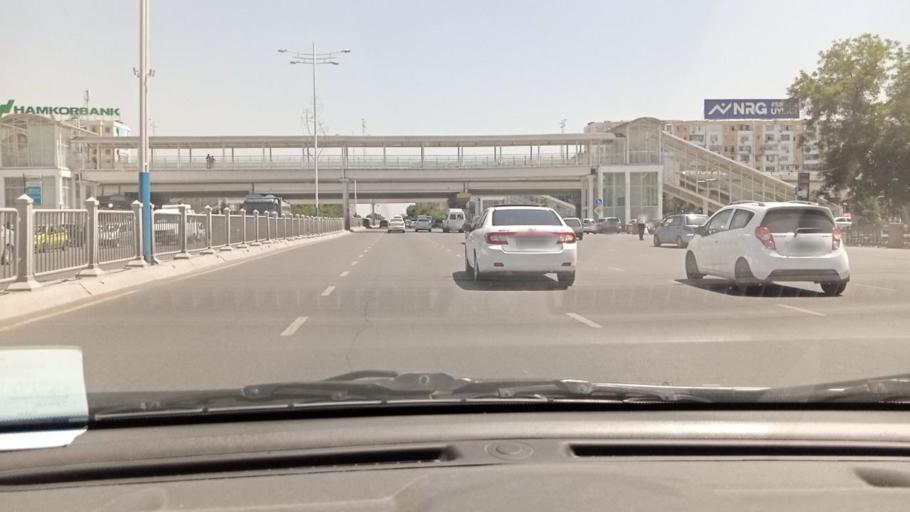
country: UZ
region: Toshkent Shahri
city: Tashkent
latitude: 41.2928
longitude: 69.2221
